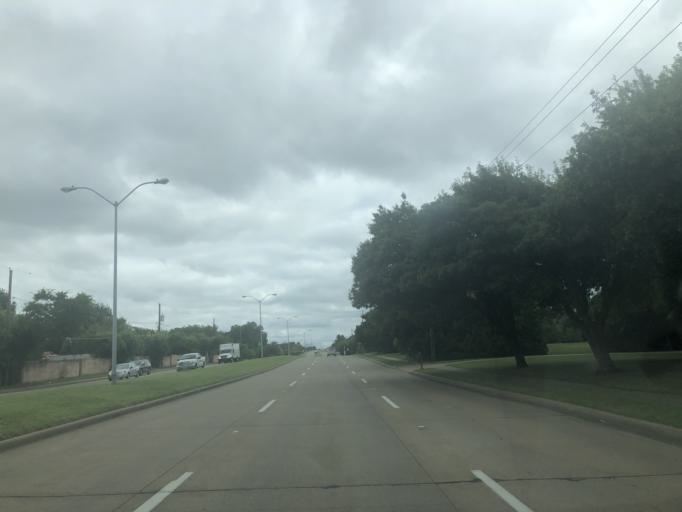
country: US
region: Texas
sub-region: Dallas County
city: Duncanville
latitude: 32.6386
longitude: -96.9427
